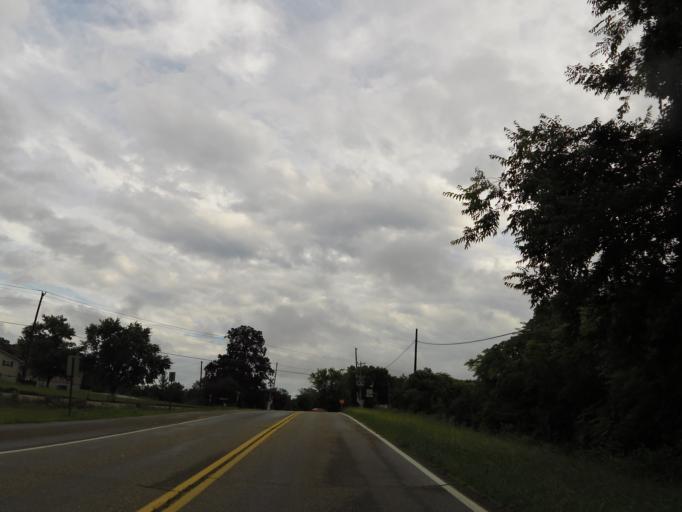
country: US
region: Tennessee
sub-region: Blount County
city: Alcoa
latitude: 35.7793
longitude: -83.9668
